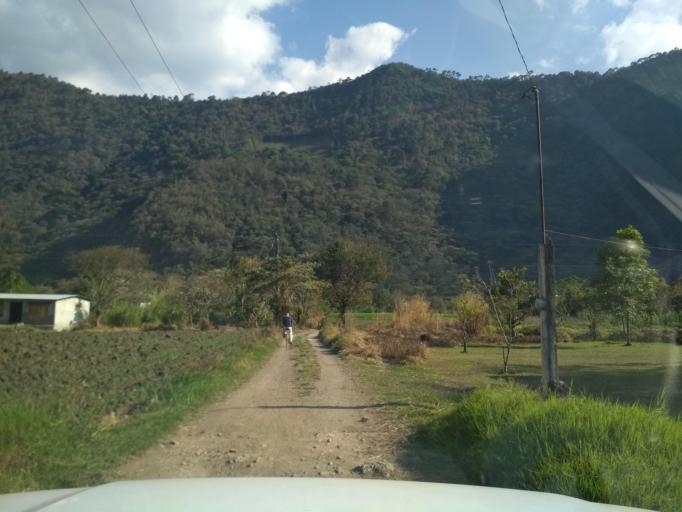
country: MX
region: Veracruz
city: Jalapilla
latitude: 18.8079
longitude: -97.0904
